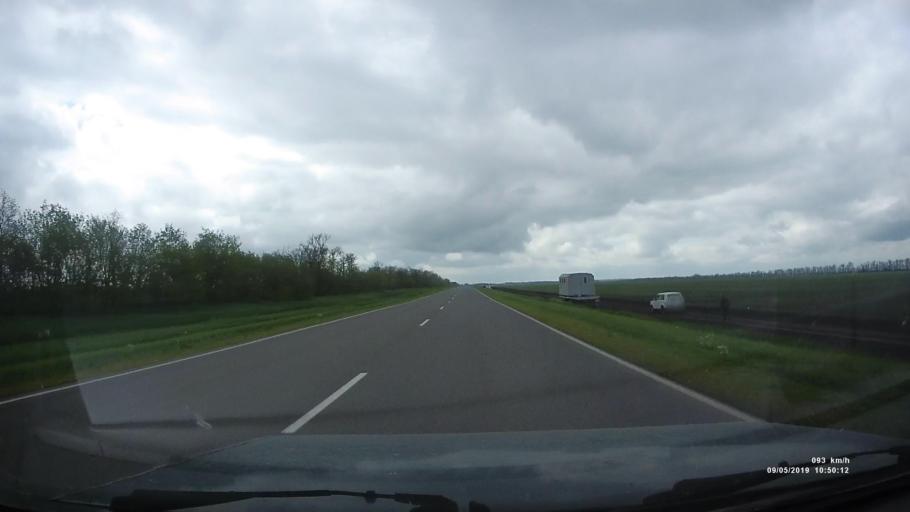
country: RU
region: Rostov
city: Peshkovo
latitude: 46.9320
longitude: 39.3554
